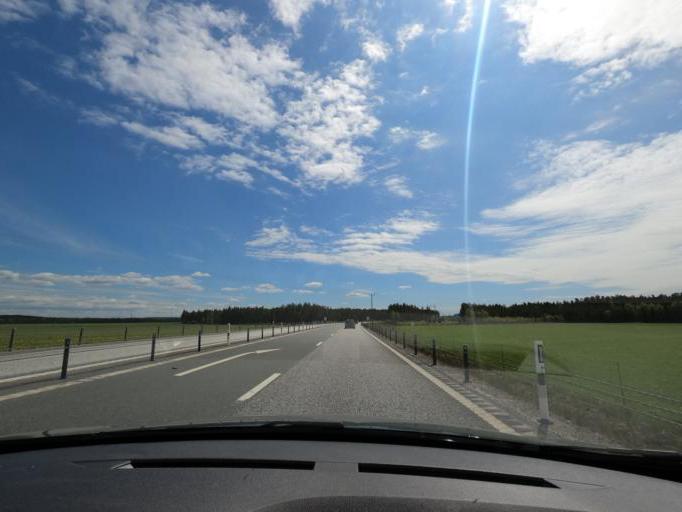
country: SE
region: Joenkoeping
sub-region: Gislaveds Kommun
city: Gislaved
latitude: 57.3137
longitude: 13.5690
